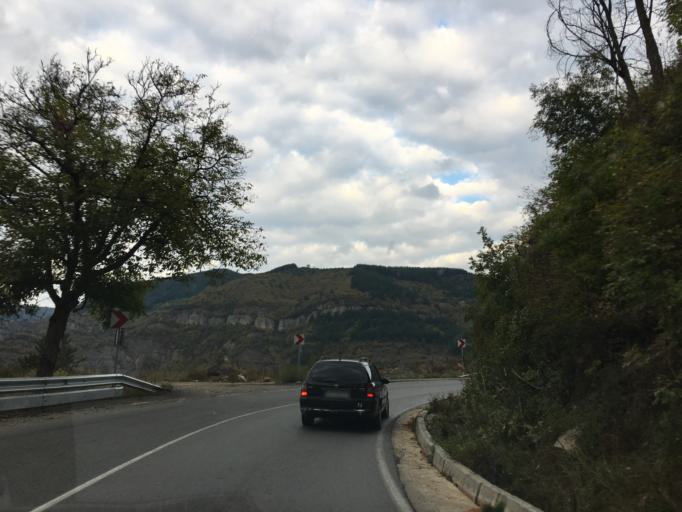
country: BG
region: Sofiya
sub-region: Obshtina Svoge
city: Svoge
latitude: 43.0010
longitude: 23.3489
